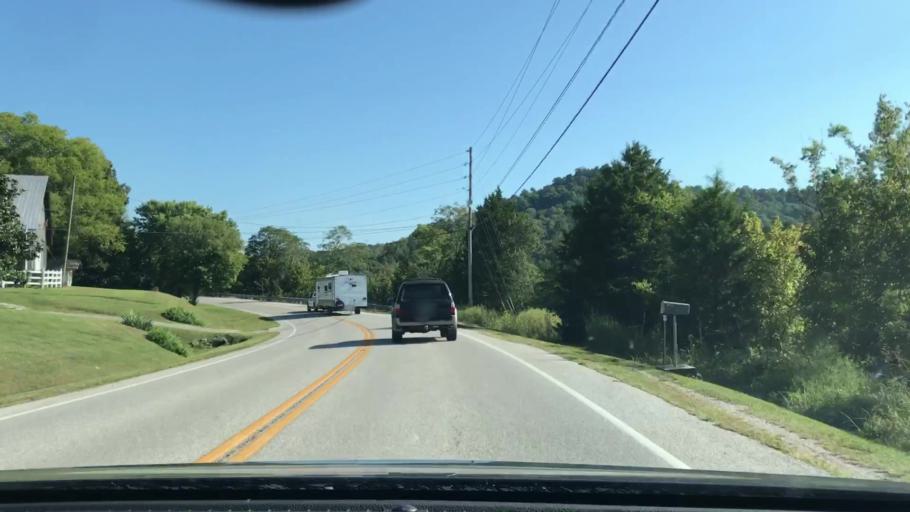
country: US
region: Tennessee
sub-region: Smith County
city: Carthage
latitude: 36.3413
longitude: -85.8989
